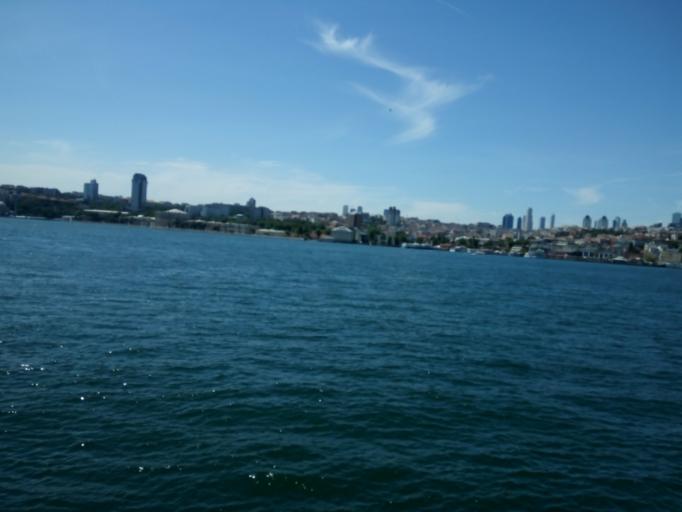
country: TR
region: Istanbul
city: UEskuedar
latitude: 41.0357
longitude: 29.0139
